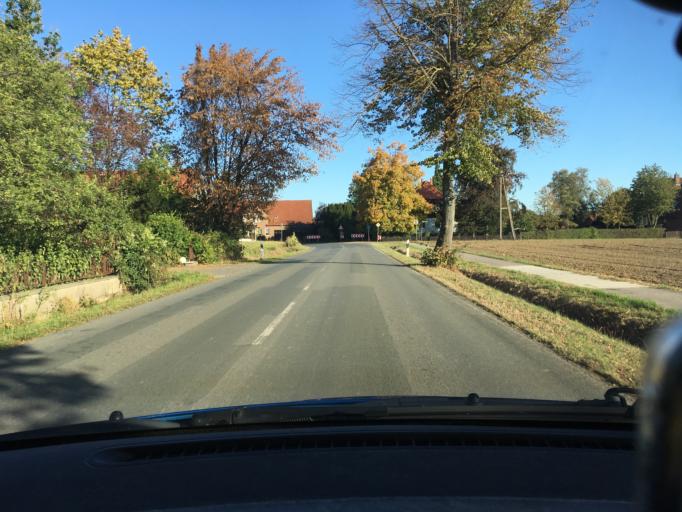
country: DE
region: Lower Saxony
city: Hulsede
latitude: 52.2225
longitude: 9.3844
